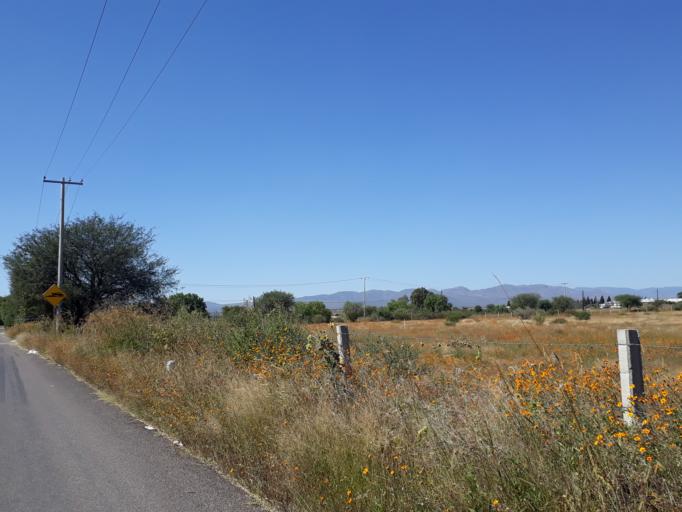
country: MX
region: Aguascalientes
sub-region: Aguascalientes
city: Penuelas (El Cienegal)
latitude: 21.7590
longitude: -102.2839
